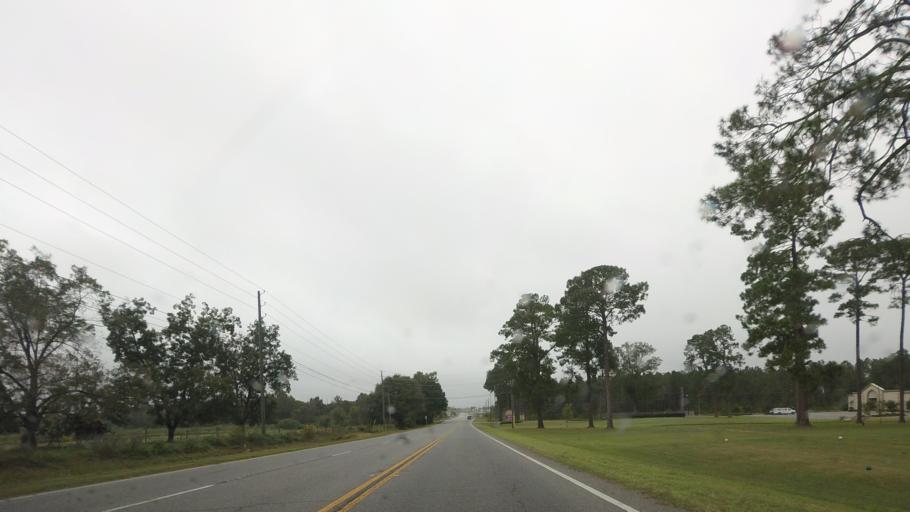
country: US
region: Georgia
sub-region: Ben Hill County
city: Fitzgerald
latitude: 31.6881
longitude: -83.2417
